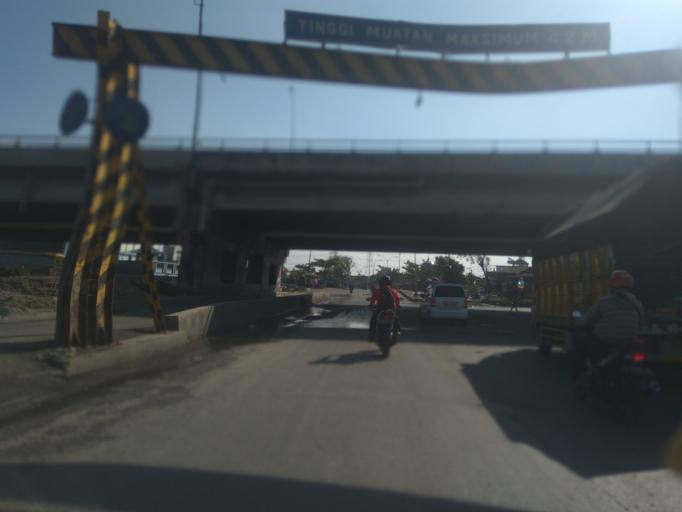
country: ID
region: Central Java
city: Semarang
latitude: -6.9572
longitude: 110.4519
